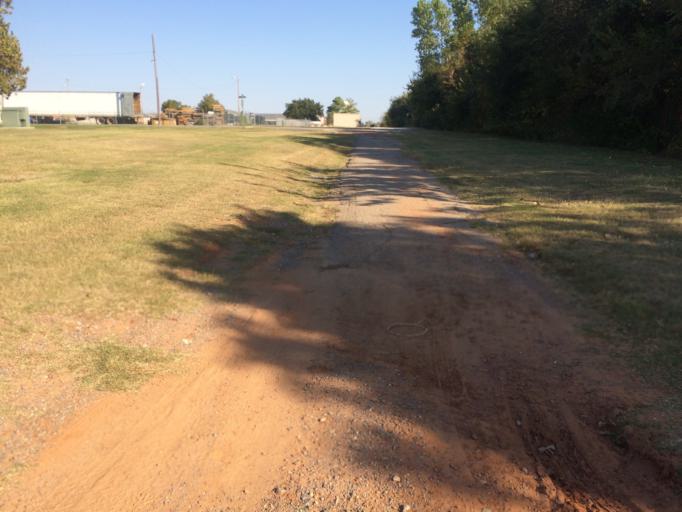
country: US
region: Oklahoma
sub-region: Cleveland County
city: Norman
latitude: 35.1845
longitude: -97.4322
